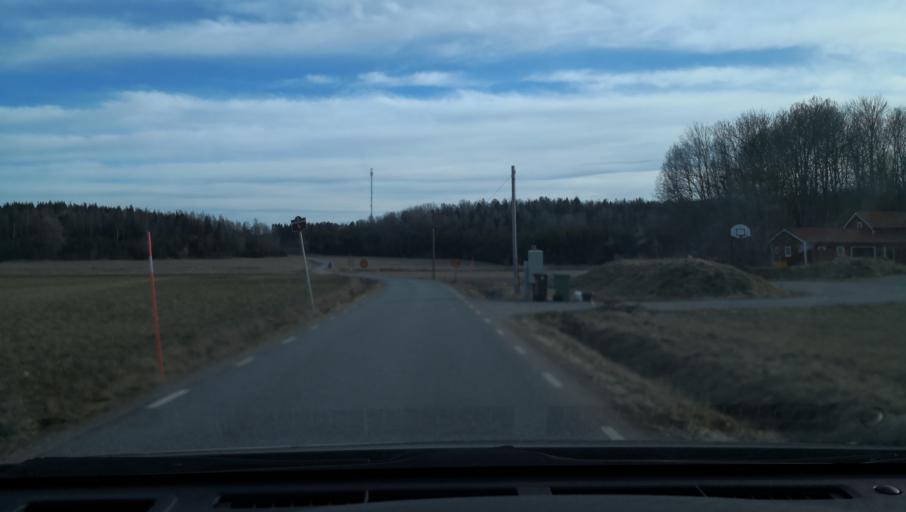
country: SE
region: Uppsala
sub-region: Enkopings Kommun
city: Grillby
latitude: 59.5481
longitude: 17.1575
